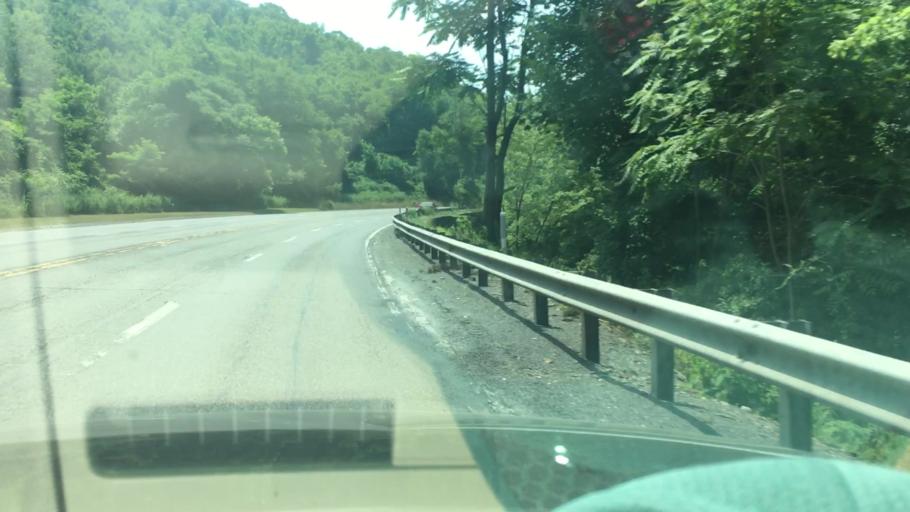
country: US
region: Pennsylvania
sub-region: Schuylkill County
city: Tamaqua
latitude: 40.7814
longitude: -75.9609
